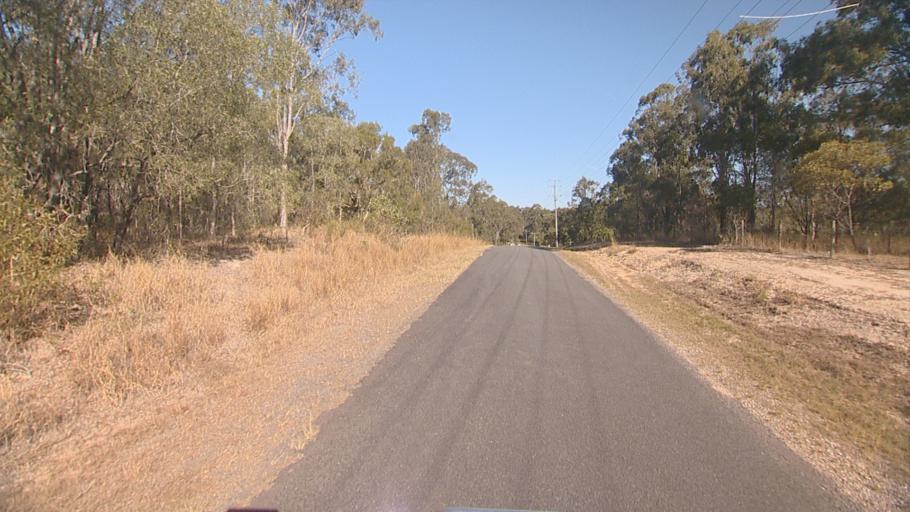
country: AU
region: Queensland
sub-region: Logan
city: Cedar Vale
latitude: -27.8604
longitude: 153.0269
